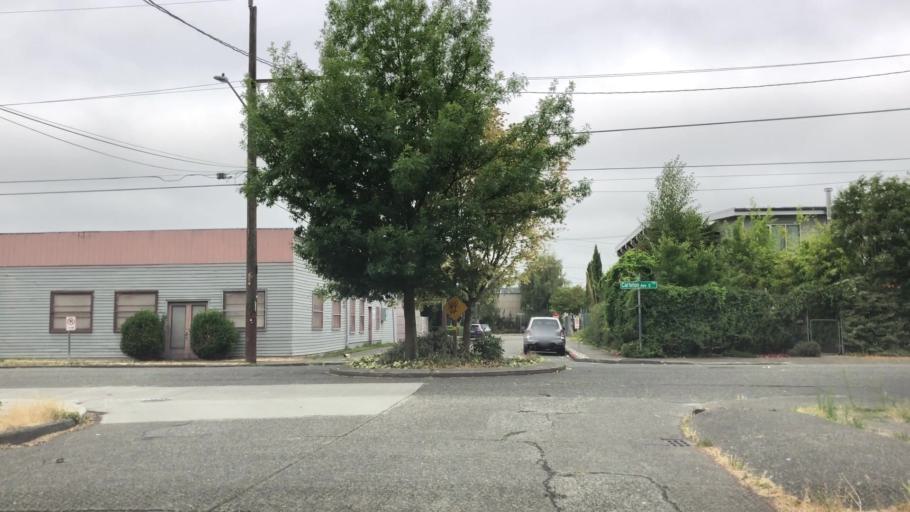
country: US
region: Washington
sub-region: King County
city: White Center
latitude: 47.5458
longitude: -122.3203
